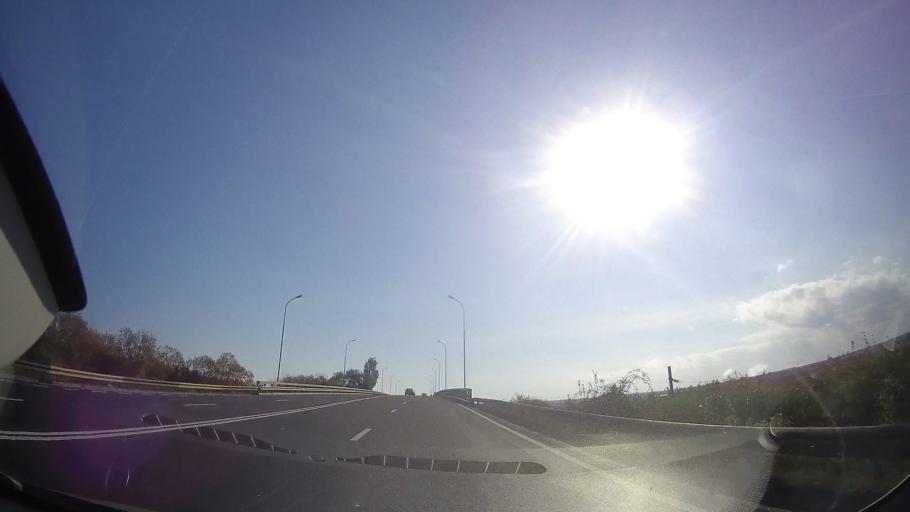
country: RO
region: Constanta
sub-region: Comuna Douazeci si Trei August
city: Dulcesti
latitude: 43.8598
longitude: 28.5756
